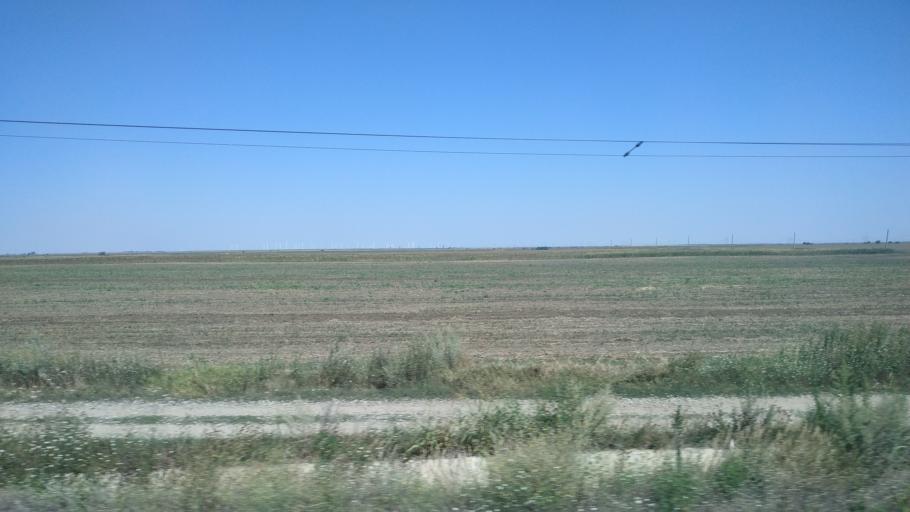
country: RO
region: Ialomita
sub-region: Municipiul Fetesti
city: Fetesti-Gara
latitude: 44.4183
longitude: 27.7747
